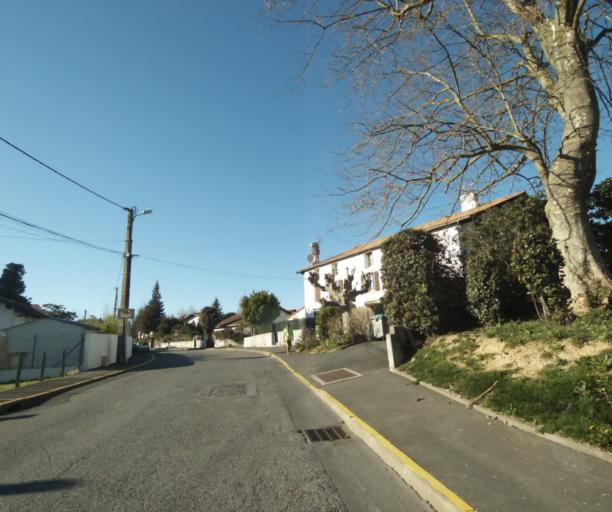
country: FR
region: Aquitaine
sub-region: Departement des Pyrenees-Atlantiques
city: Hendaye
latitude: 43.3621
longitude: -1.7567
